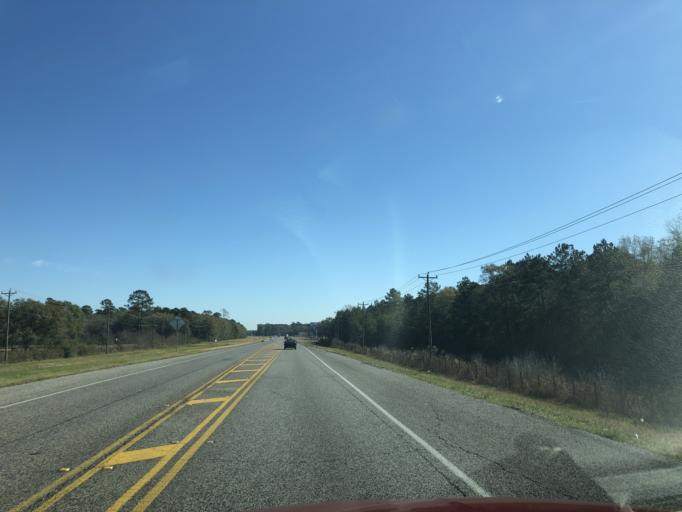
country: US
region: Texas
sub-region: Montgomery County
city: Porter Heights
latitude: 30.2171
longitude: -95.2741
